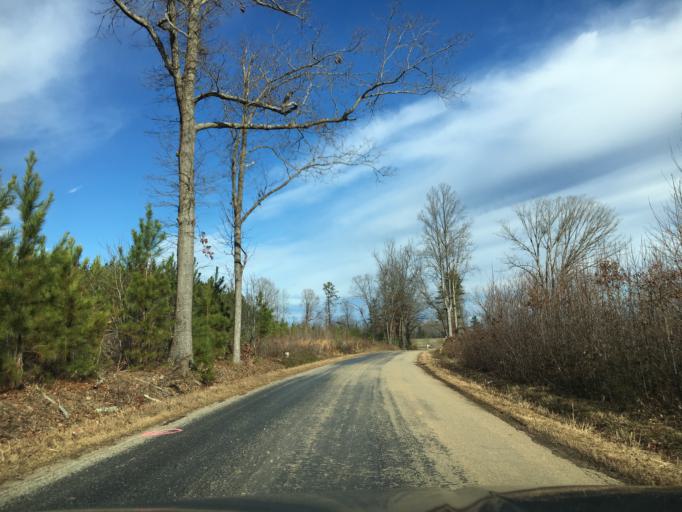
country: US
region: Virginia
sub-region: Nottoway County
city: Crewe
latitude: 37.2723
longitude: -78.2175
